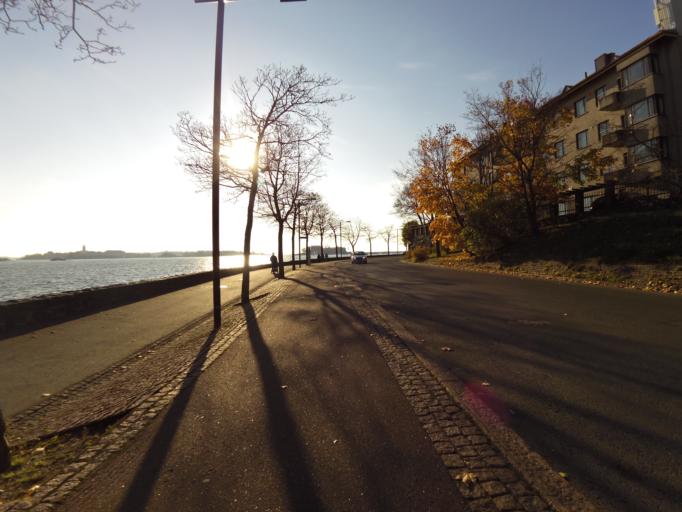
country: FI
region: Uusimaa
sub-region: Helsinki
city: Helsinki
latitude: 60.1568
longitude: 24.9628
